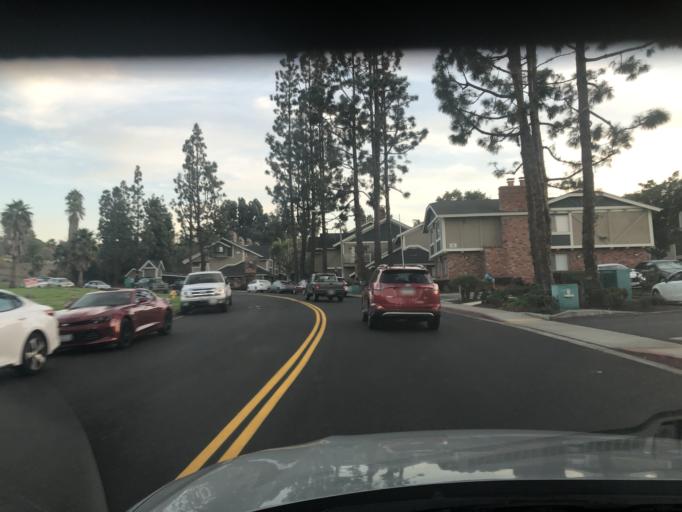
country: US
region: California
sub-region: San Diego County
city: Chula Vista
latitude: 32.6470
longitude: -117.0639
